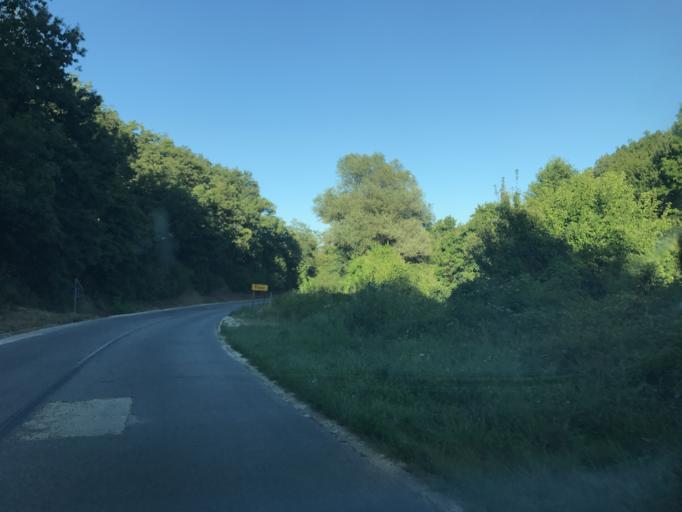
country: RO
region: Mehedinti
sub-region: Comuna Gogosu
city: Ostrovu Mare
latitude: 44.2905
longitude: 22.3330
